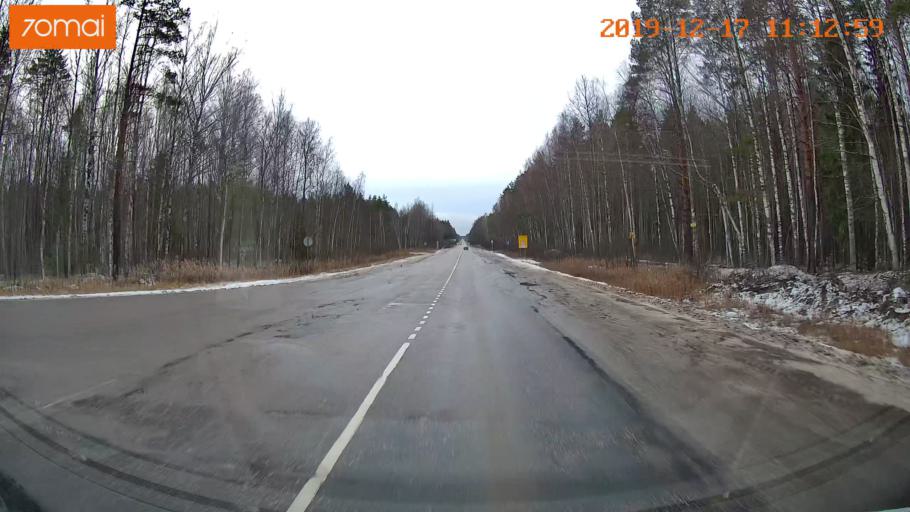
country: RU
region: Vladimir
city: Gus'-Khrustal'nyy
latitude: 55.5689
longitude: 40.6231
